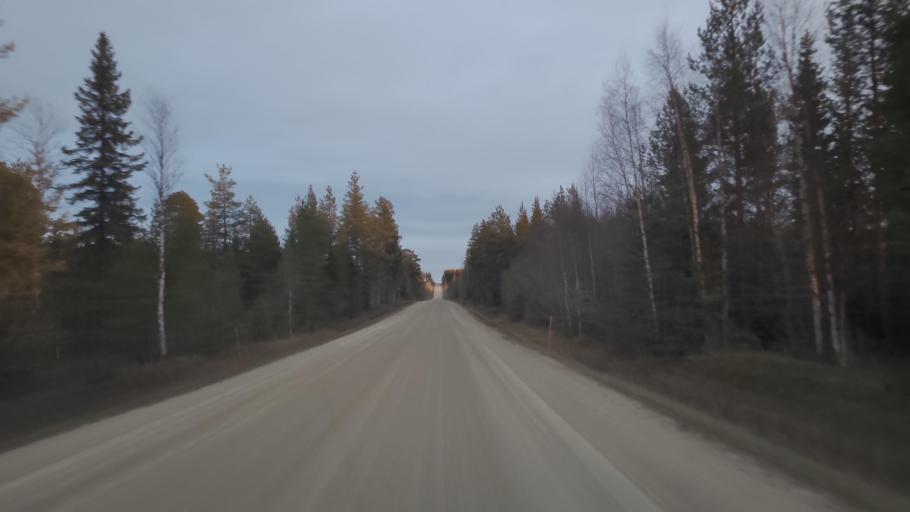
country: FI
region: Lapland
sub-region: Kemi-Tornio
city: Tervola
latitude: 66.0634
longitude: 24.9195
